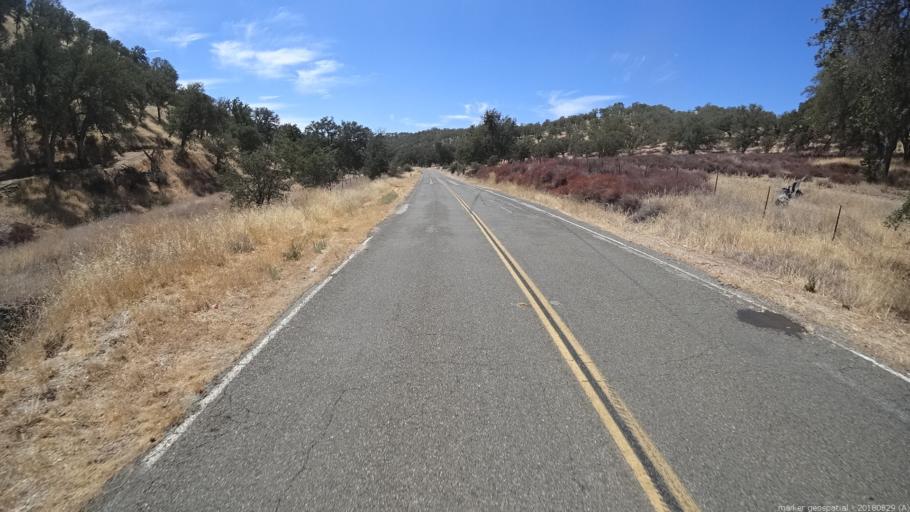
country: US
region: California
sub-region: San Luis Obispo County
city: Lake Nacimiento
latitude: 35.9133
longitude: -121.0871
